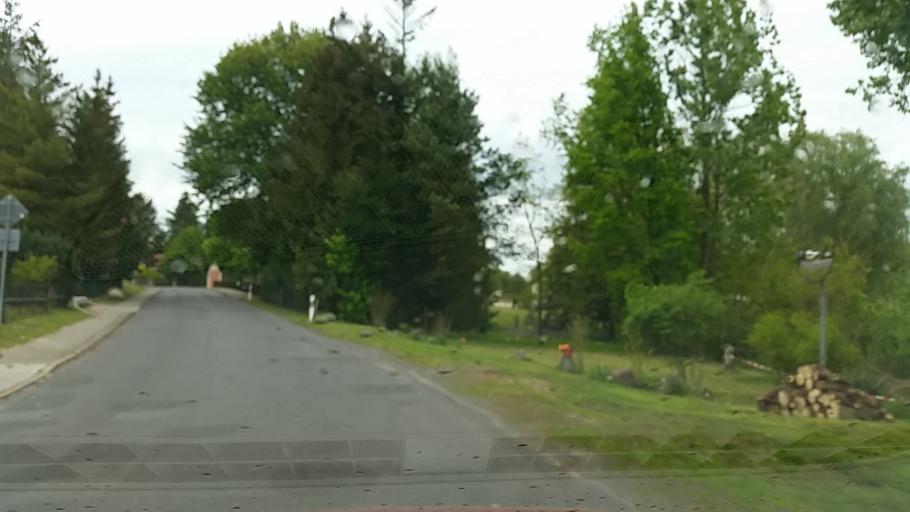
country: DE
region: Brandenburg
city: Reichenwalde
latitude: 52.2897
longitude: 13.9885
